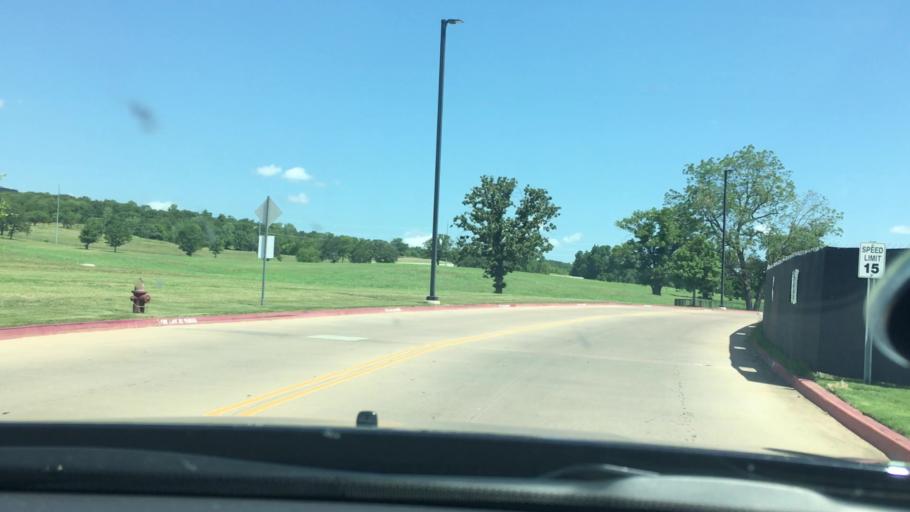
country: US
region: Oklahoma
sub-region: Pontotoc County
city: Ada
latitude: 34.7319
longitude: -96.6480
